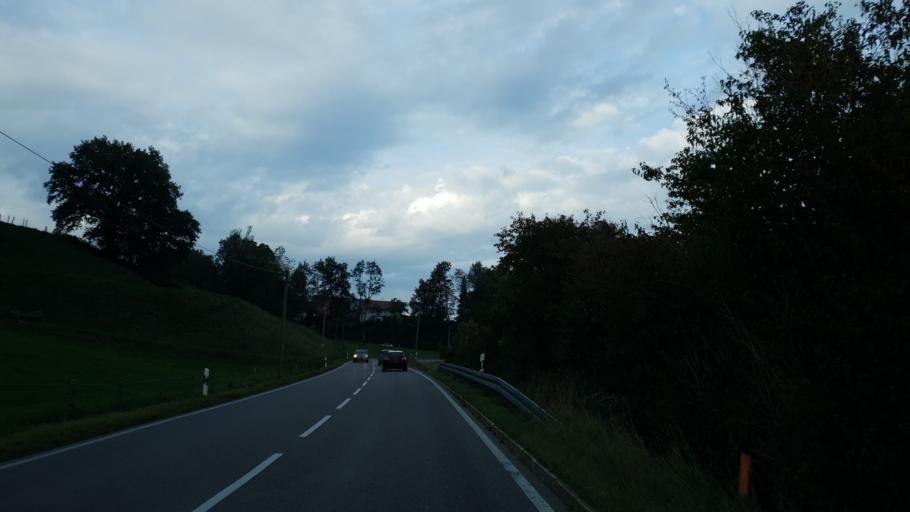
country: DE
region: Bavaria
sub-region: Swabia
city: Gestratz
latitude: 47.6601
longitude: 9.9388
